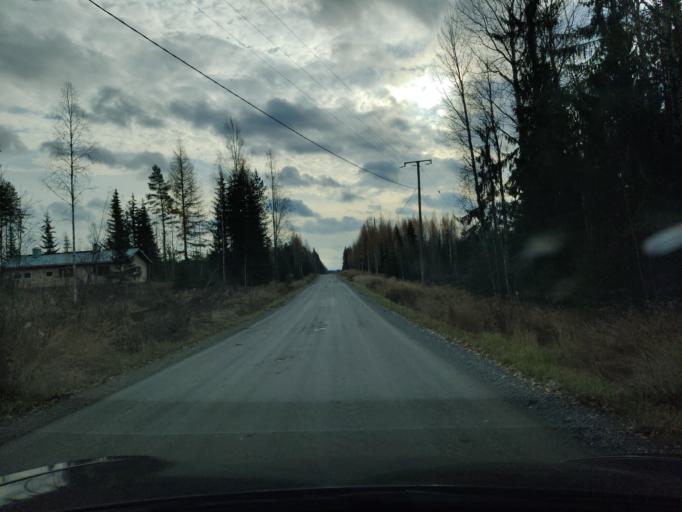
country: FI
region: Northern Savo
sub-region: Kuopio
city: Siilinjaervi
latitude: 63.1136
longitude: 27.5472
